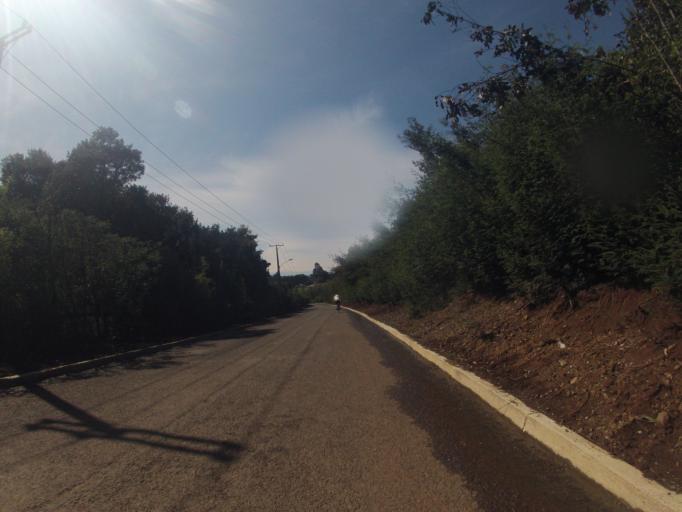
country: CL
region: Araucania
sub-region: Provincia de Cautin
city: Temuco
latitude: -38.6897
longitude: -72.5558
